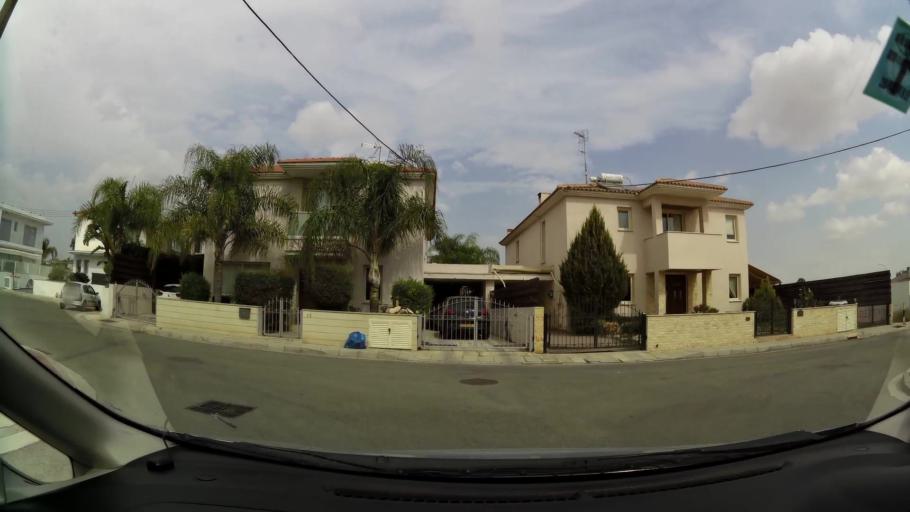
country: CY
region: Lefkosia
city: Geri
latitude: 35.0821
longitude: 33.3880
